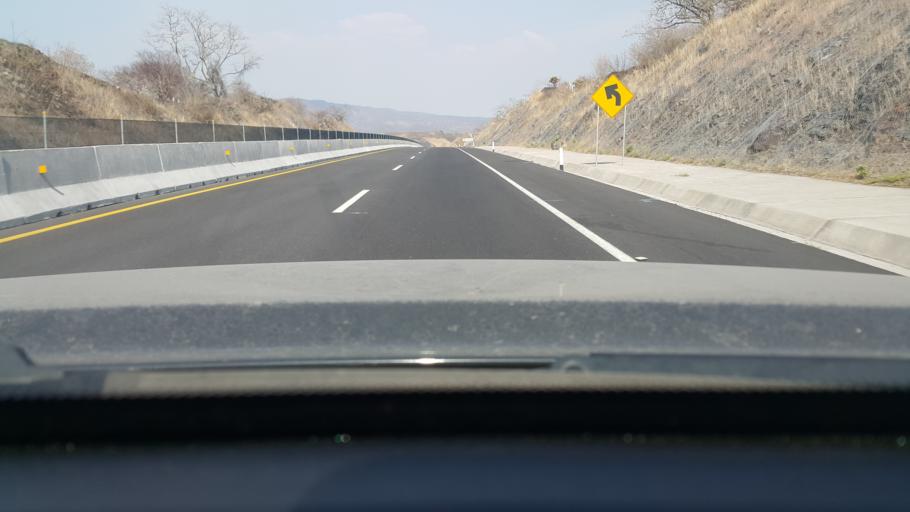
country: MX
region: Nayarit
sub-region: Ahuacatlan
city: Ahuacatlan
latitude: 21.0671
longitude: -104.4685
